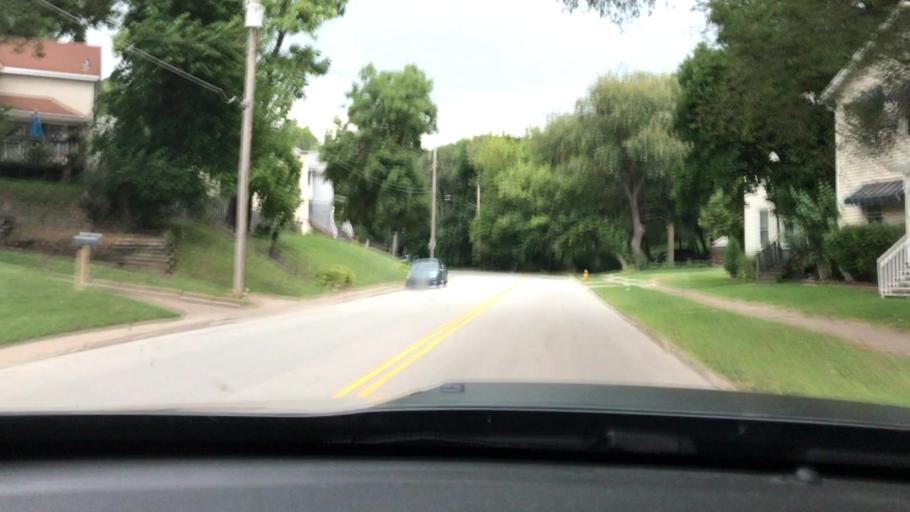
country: US
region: Iowa
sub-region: Scott County
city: Bettendorf
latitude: 41.5339
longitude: -90.5427
